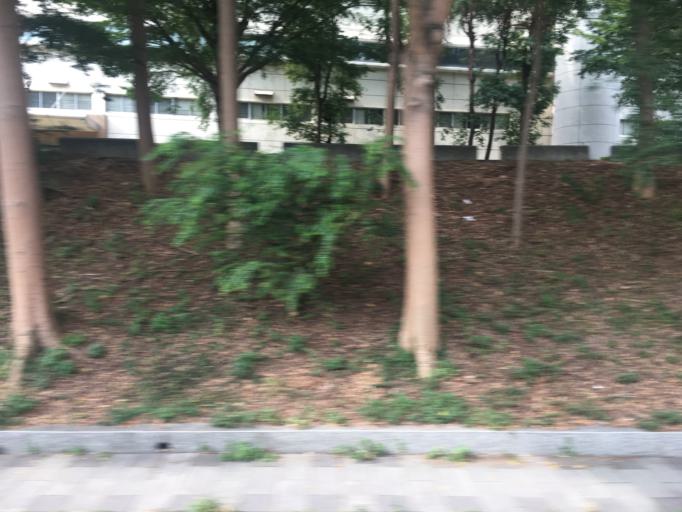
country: TW
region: Taiwan
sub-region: Hsinchu
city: Hsinchu
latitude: 24.7822
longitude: 120.9996
